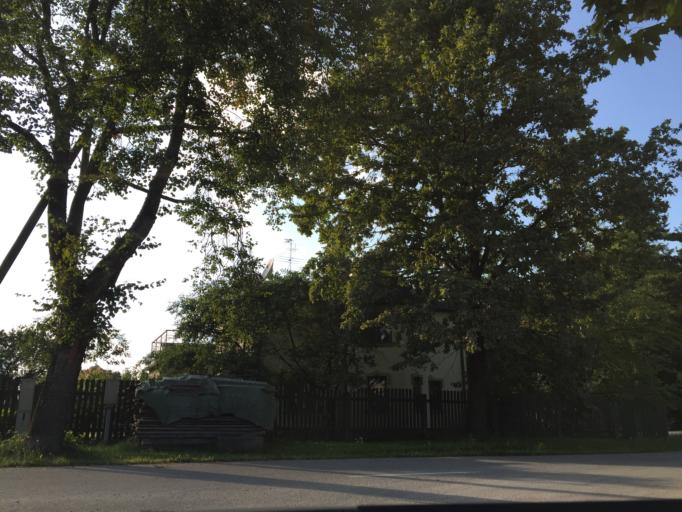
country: LV
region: Ikskile
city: Ikskile
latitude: 56.8377
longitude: 24.5103
